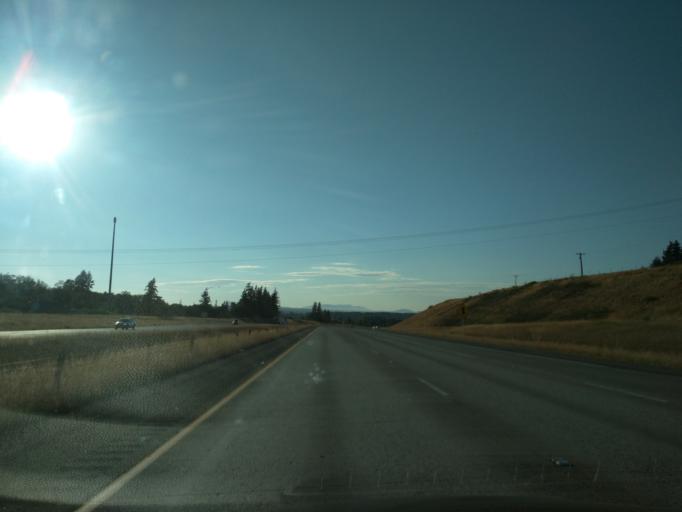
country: US
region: Washington
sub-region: Snohomish County
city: Stanwood
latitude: 48.3085
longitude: -122.3168
